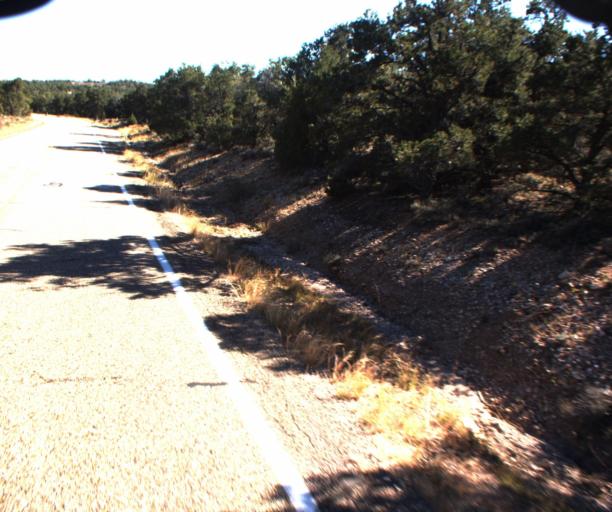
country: US
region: Arizona
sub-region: Coconino County
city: Fredonia
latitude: 36.7453
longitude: -112.1162
